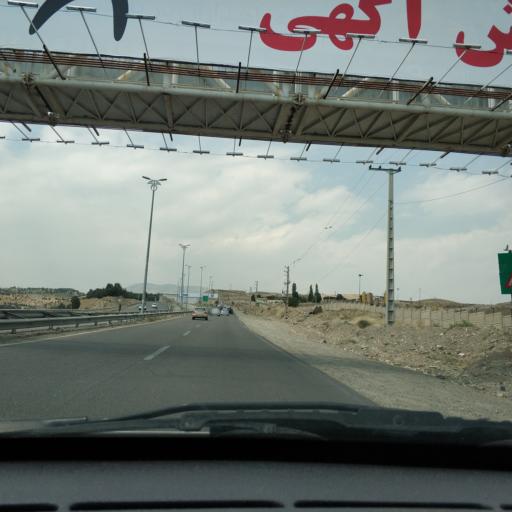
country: IR
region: Tehran
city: Tajrish
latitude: 35.7809
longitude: 51.5634
